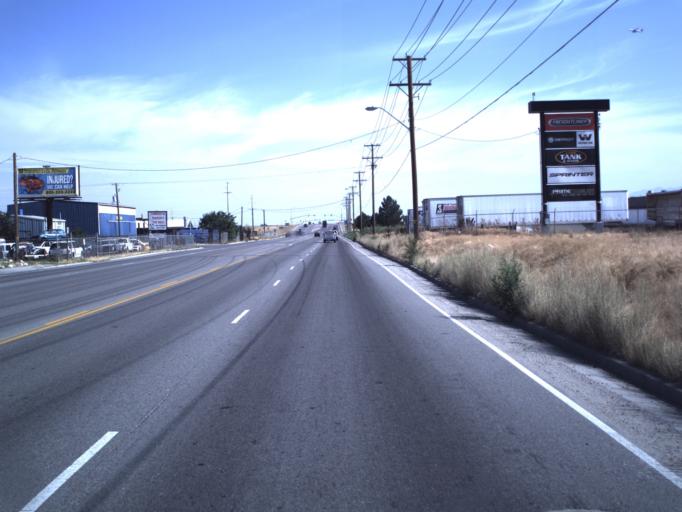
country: US
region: Utah
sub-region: Salt Lake County
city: West Valley City
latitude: 40.7189
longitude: -112.0248
